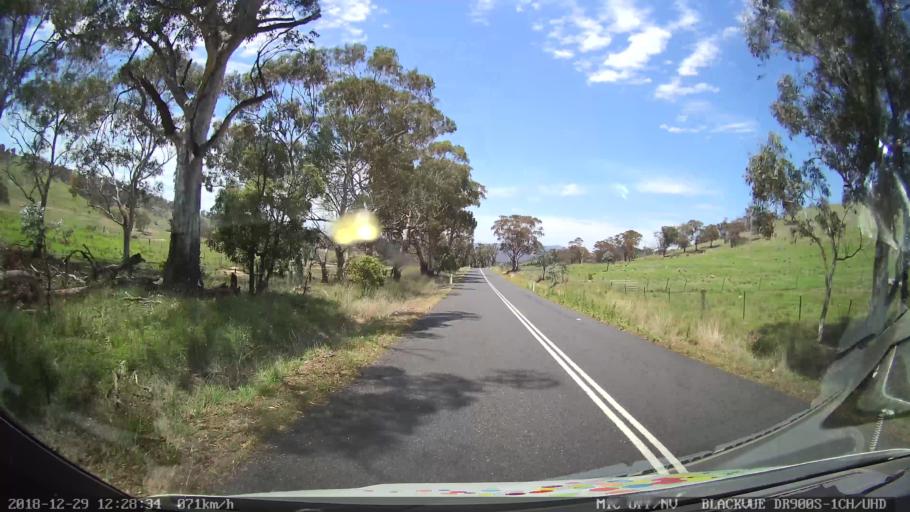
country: AU
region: Australian Capital Territory
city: Macarthur
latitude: -35.4881
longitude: 149.2265
